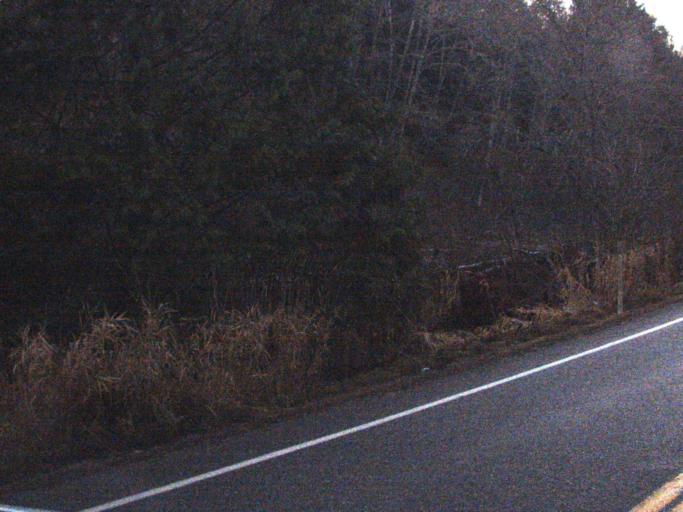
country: US
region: Washington
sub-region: Skagit County
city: Big Lake
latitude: 48.3313
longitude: -122.2755
